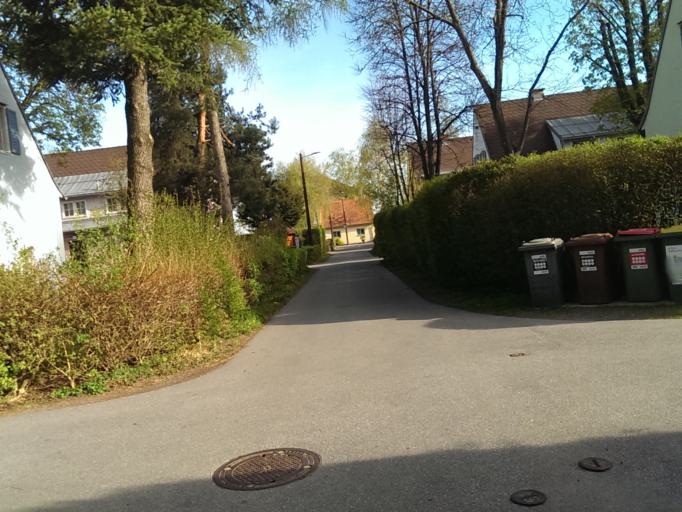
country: AT
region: Styria
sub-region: Graz Stadt
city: Graz
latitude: 47.0450
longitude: 15.4468
